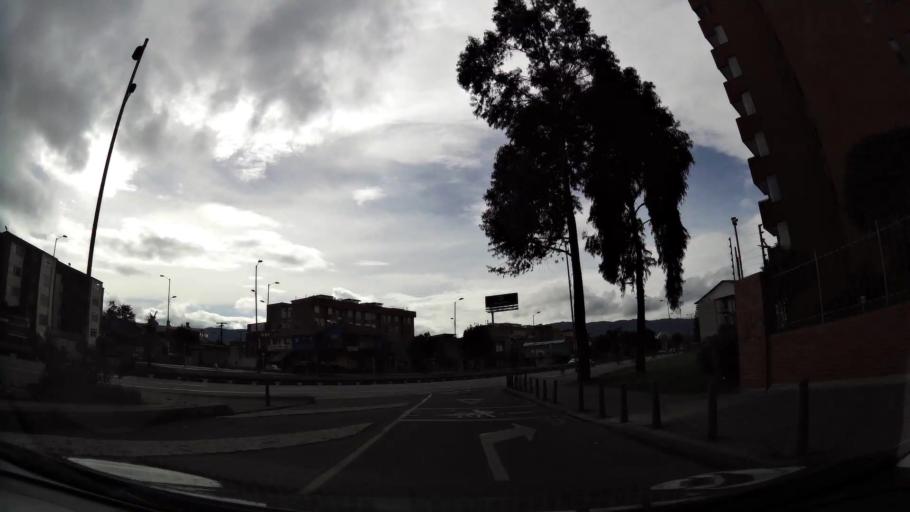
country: CO
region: Bogota D.C.
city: Barrio San Luis
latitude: 4.7177
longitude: -74.0739
